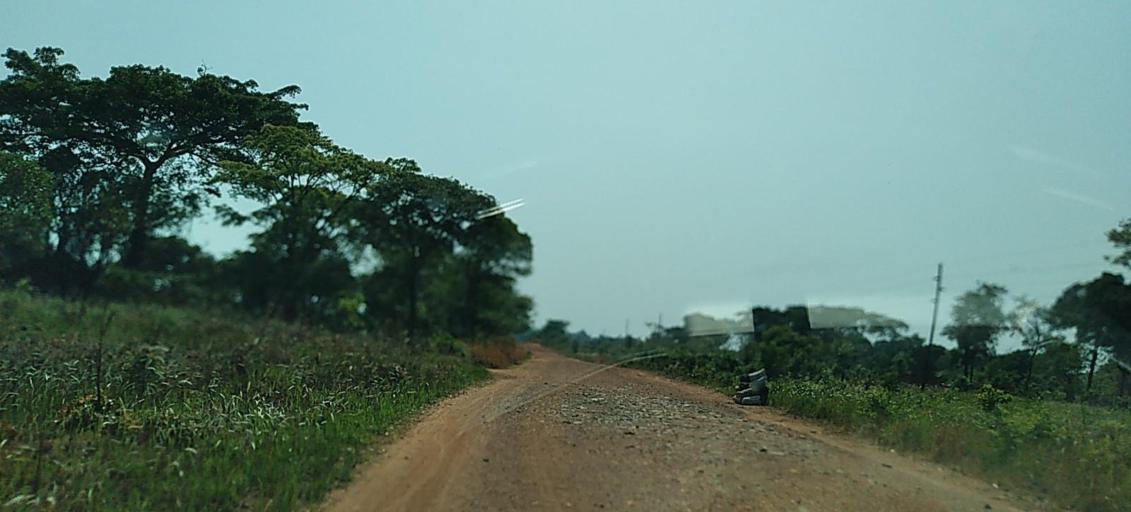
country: ZM
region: North-Western
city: Kansanshi
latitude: -12.0066
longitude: 26.5261
